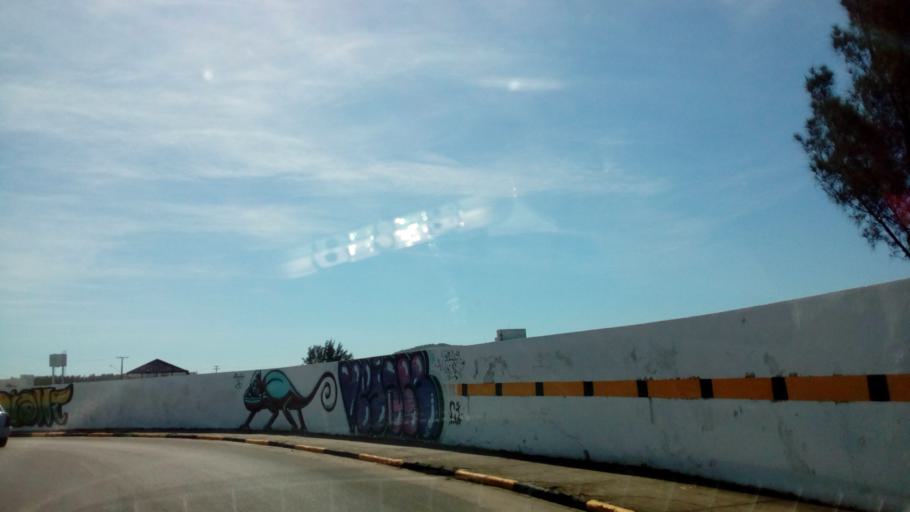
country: BR
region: Santa Catarina
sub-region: Laguna
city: Laguna
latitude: -28.4960
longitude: -48.7743
